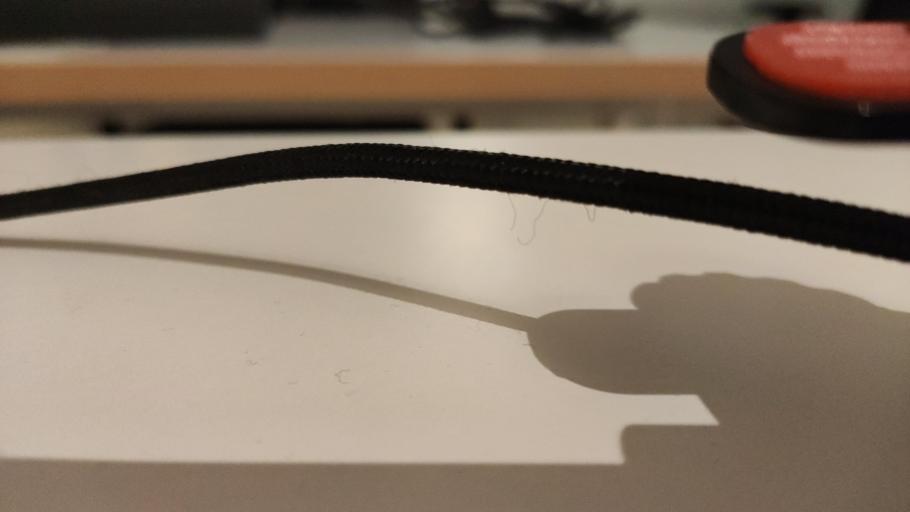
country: RU
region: Moskovskaya
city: Novoye
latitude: 55.6082
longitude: 38.9281
